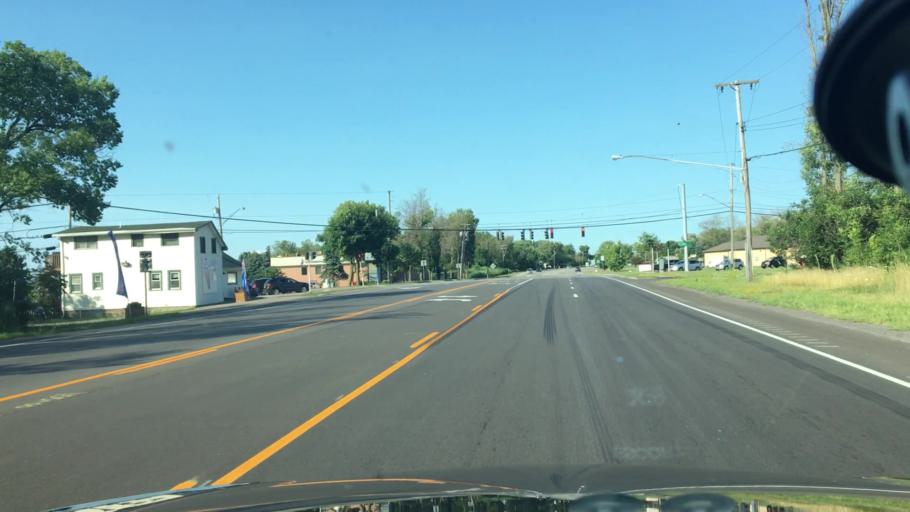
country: US
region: New York
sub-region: Erie County
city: Wanakah
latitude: 42.7349
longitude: -78.8802
